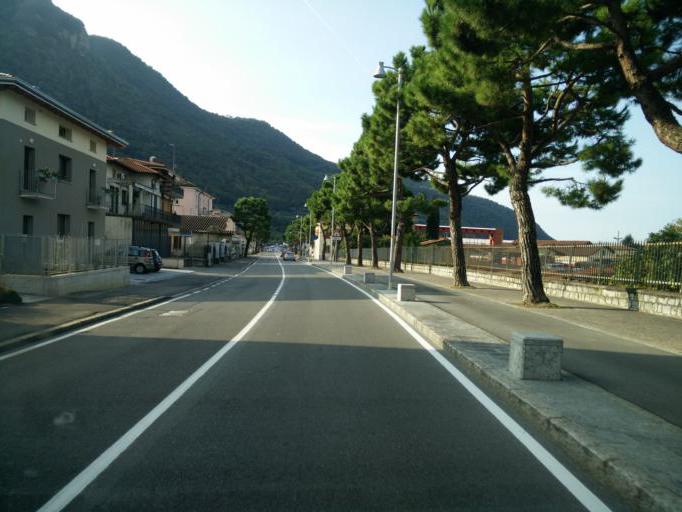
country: IT
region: Lombardy
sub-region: Provincia di Brescia
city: Iseo
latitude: 45.6568
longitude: 10.0509
